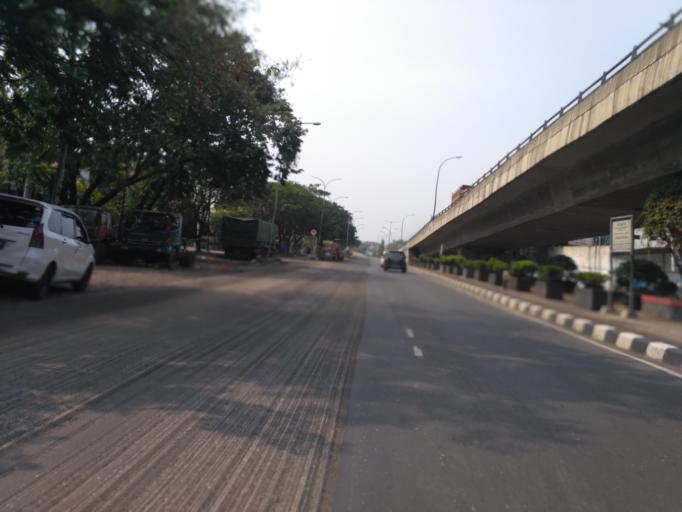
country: ID
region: Central Java
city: Semarang
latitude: -6.9839
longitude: 110.3846
